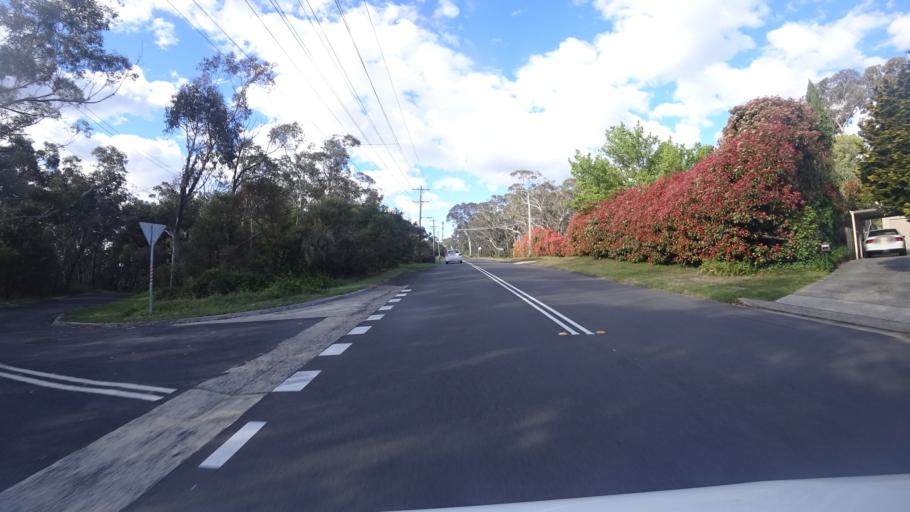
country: AU
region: New South Wales
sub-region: Blue Mountains Municipality
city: Katoomba
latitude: -33.7123
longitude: 150.2984
